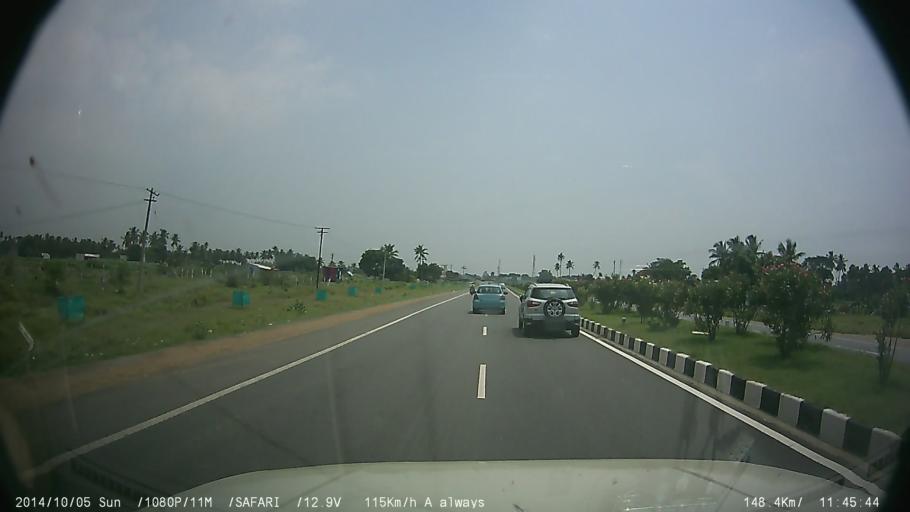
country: IN
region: Tamil Nadu
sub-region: Salem
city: Attur
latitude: 11.5916
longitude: 78.6592
